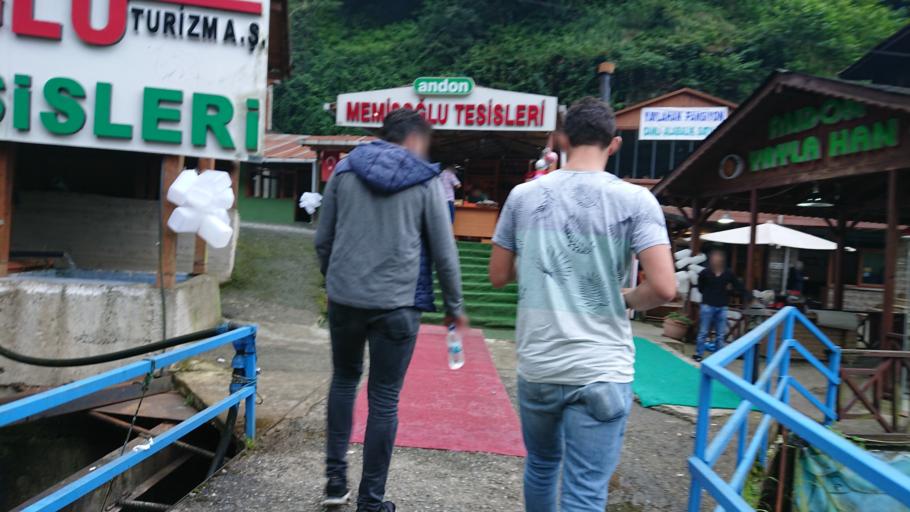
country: TR
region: Rize
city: Ikizdere
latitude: 40.8599
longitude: 40.5863
